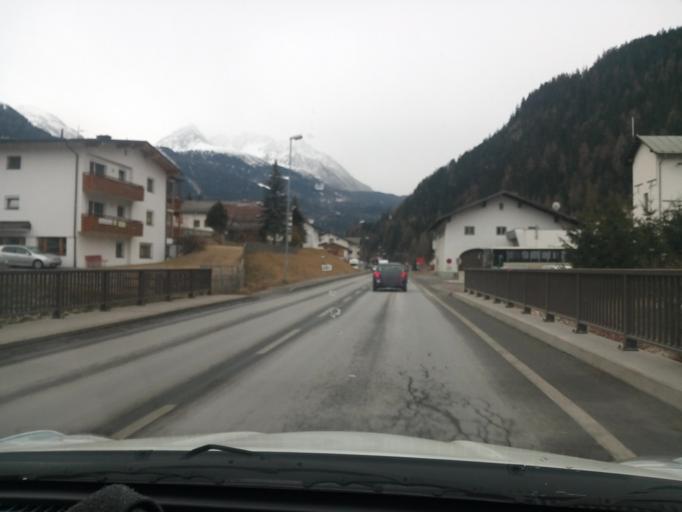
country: AT
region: Tyrol
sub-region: Politischer Bezirk Landeck
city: Nauders
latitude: 46.8907
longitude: 10.4991
